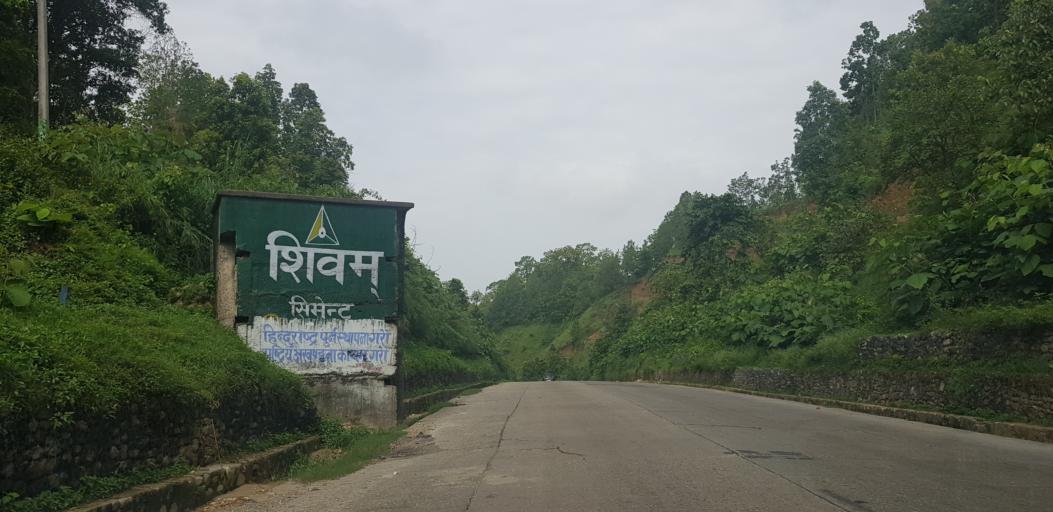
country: NP
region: Central Region
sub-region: Narayani Zone
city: Hitura
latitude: 27.3619
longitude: 85.0053
